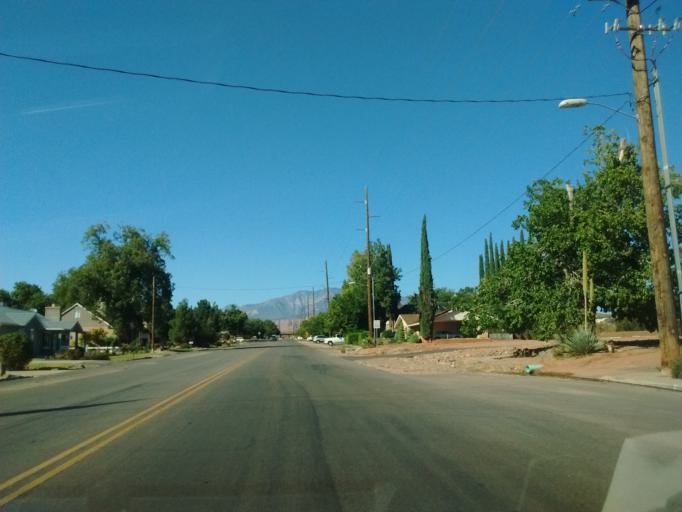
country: US
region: Utah
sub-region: Washington County
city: Washington
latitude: 37.1318
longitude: -113.5098
